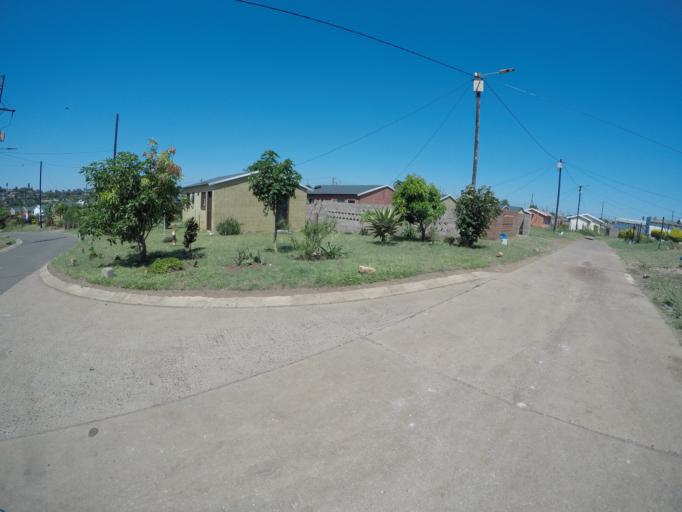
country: ZA
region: KwaZulu-Natal
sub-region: uThungulu District Municipality
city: Empangeni
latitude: -28.7639
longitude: 31.8783
